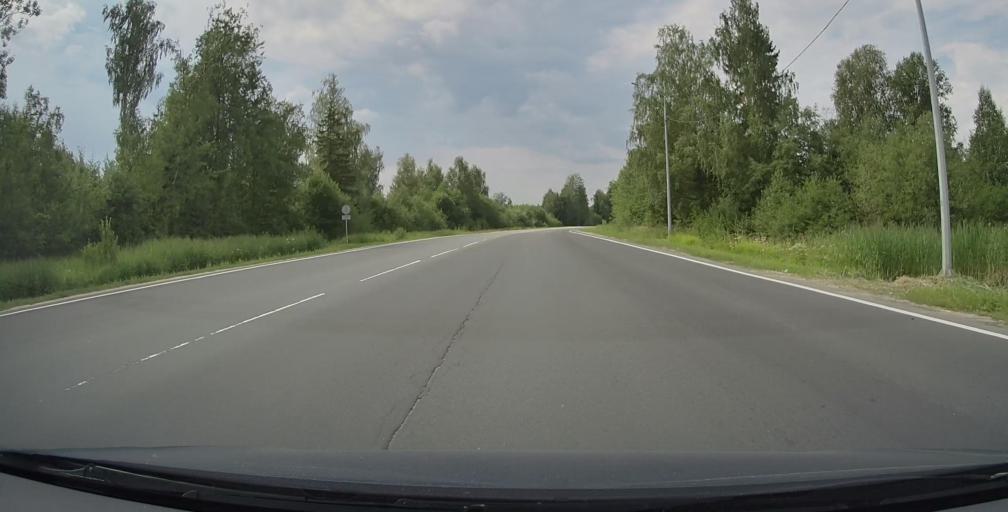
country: RU
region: Jaroslavl
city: Tutayev
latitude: 57.8845
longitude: 39.4445
